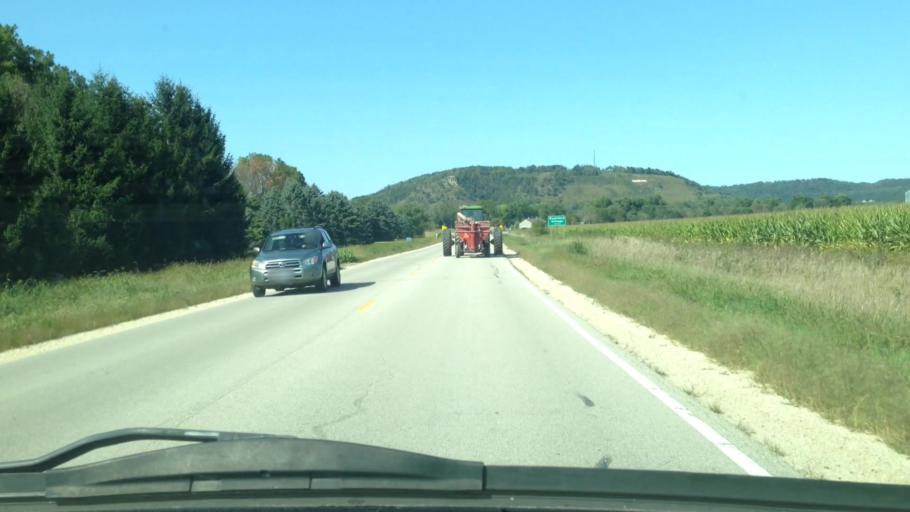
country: US
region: Minnesota
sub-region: Fillmore County
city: Rushford
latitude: 43.7876
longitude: -91.7654
